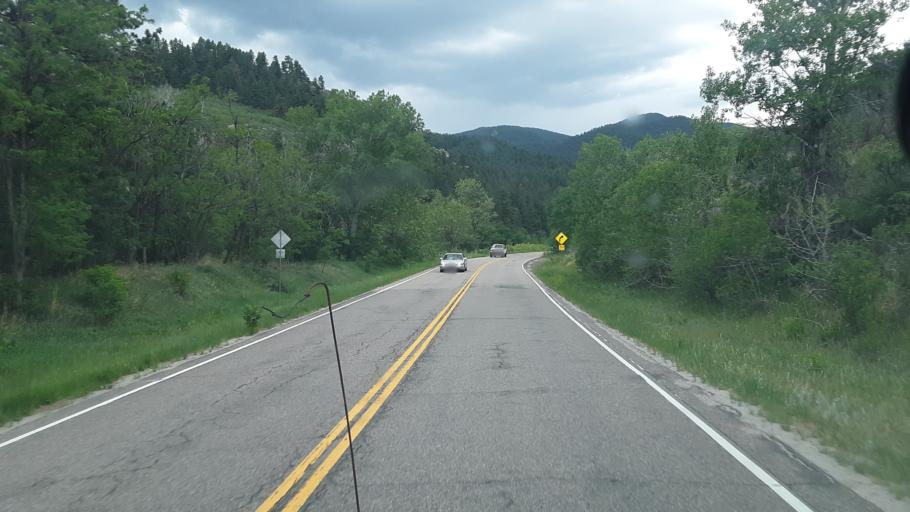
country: US
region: Colorado
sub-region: Fremont County
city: Florence
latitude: 38.1812
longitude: -105.1094
